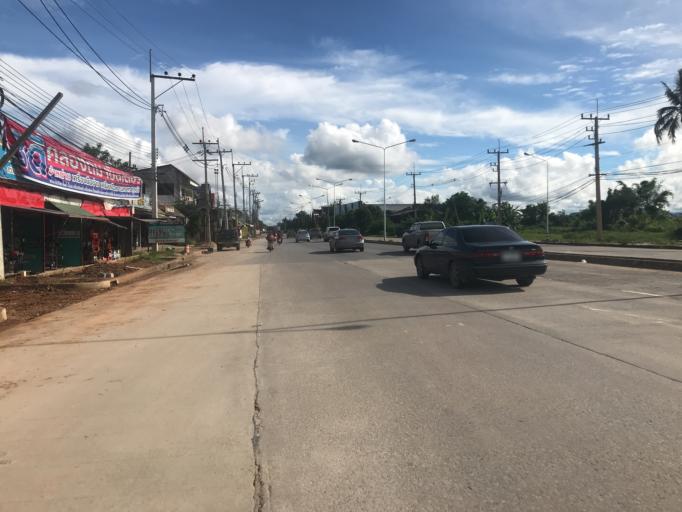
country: TH
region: Chiang Rai
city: Chiang Rai
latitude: 19.9592
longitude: 99.8530
